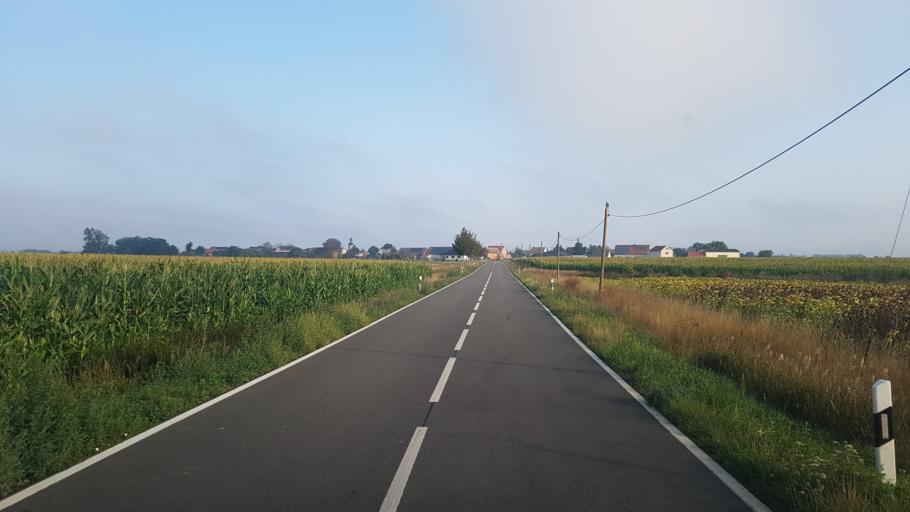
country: DE
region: Saxony
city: Dommitzsch
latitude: 51.7038
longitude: 12.8749
